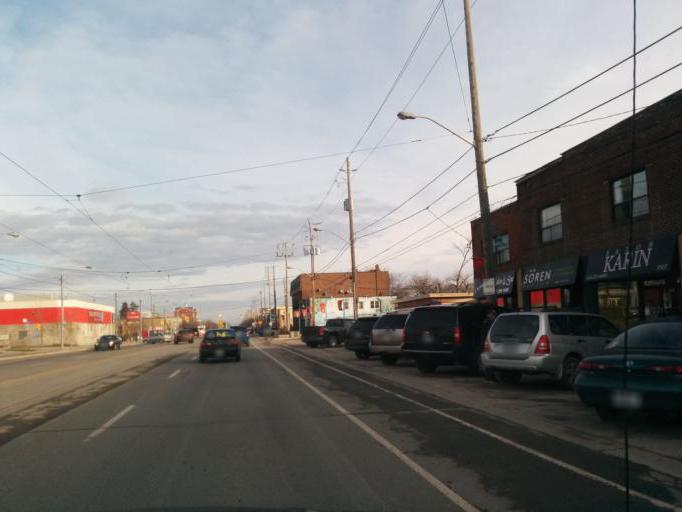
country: CA
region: Ontario
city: Etobicoke
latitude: 43.5948
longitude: -79.5320
